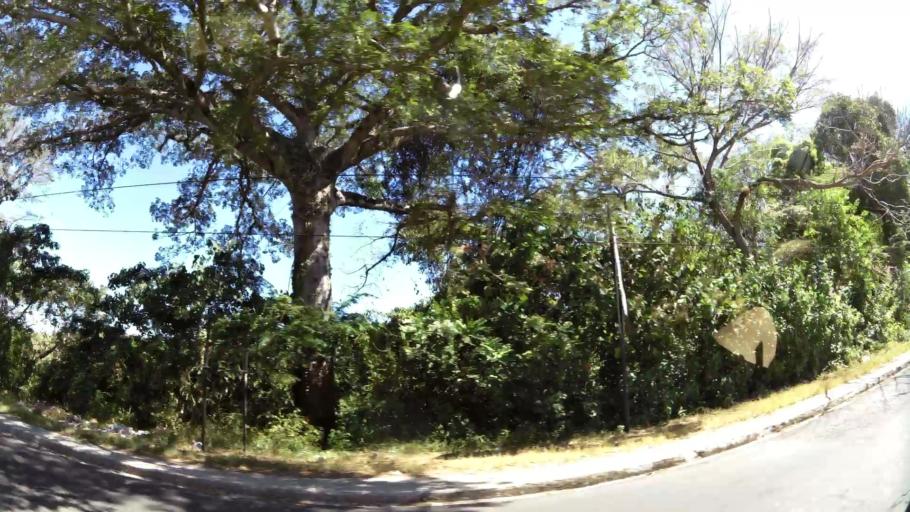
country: SV
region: La Libertad
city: San Juan Opico
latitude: 13.8654
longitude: -89.3591
